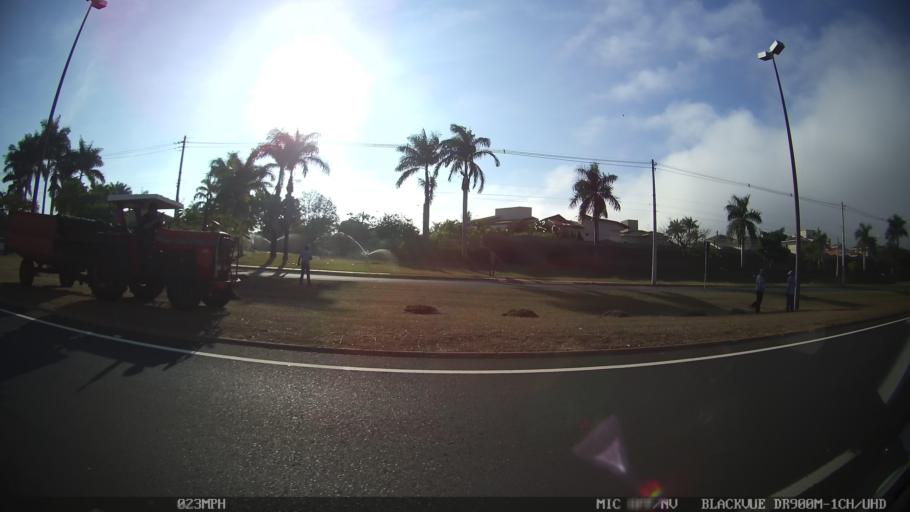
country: BR
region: Sao Paulo
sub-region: Sao Jose Do Rio Preto
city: Sao Jose do Rio Preto
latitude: -20.8215
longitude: -49.3449
